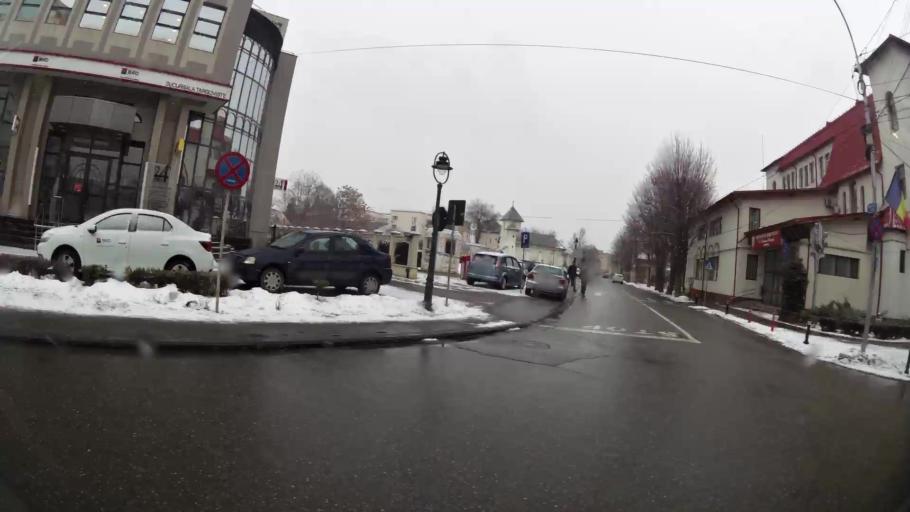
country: RO
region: Dambovita
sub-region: Municipiul Targoviste
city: Targoviste
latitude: 44.9284
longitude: 25.4608
